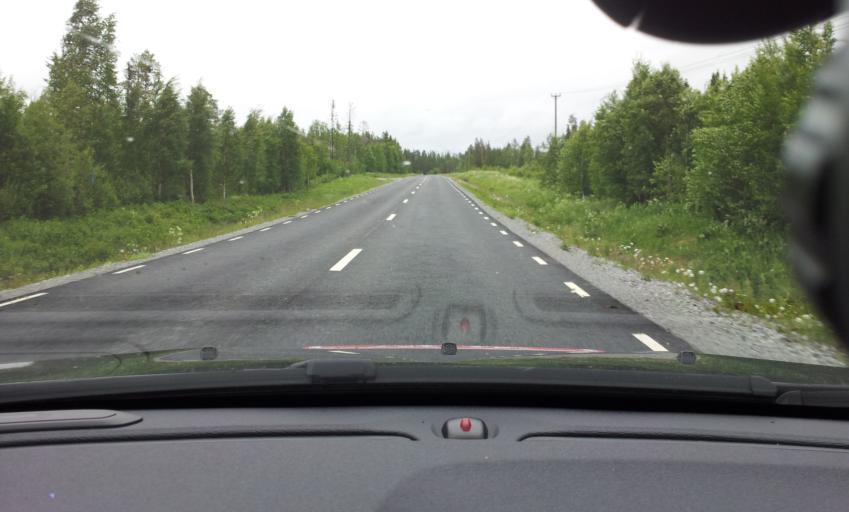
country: SE
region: Jaemtland
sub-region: OEstersunds Kommun
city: Lit
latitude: 63.7381
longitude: 14.7661
